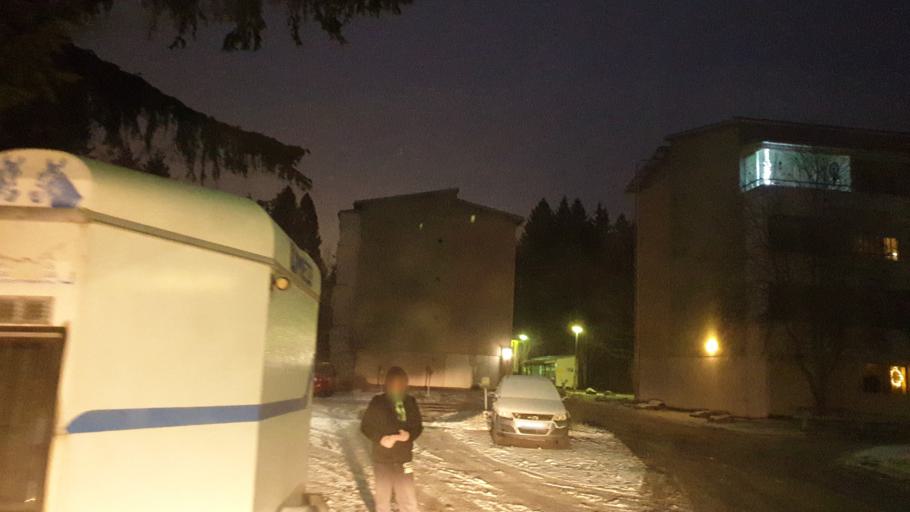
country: FI
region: Southern Savonia
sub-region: Savonlinna
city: Savonlinna
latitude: 61.8607
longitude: 28.9527
